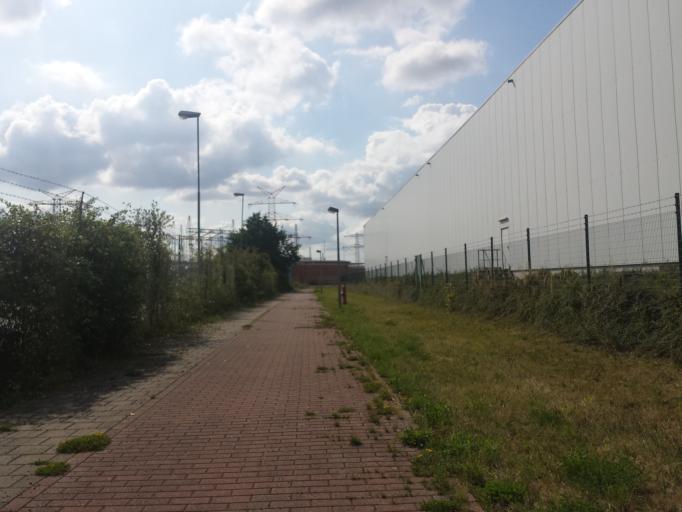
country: DE
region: Lower Saxony
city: Stuhr
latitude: 53.0931
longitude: 8.6983
